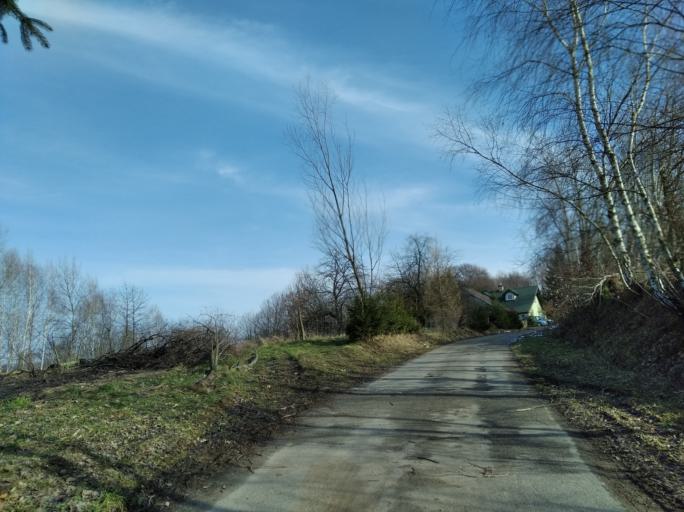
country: PL
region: Subcarpathian Voivodeship
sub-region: Powiat brzozowski
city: Gorki
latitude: 49.6448
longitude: 22.0537
